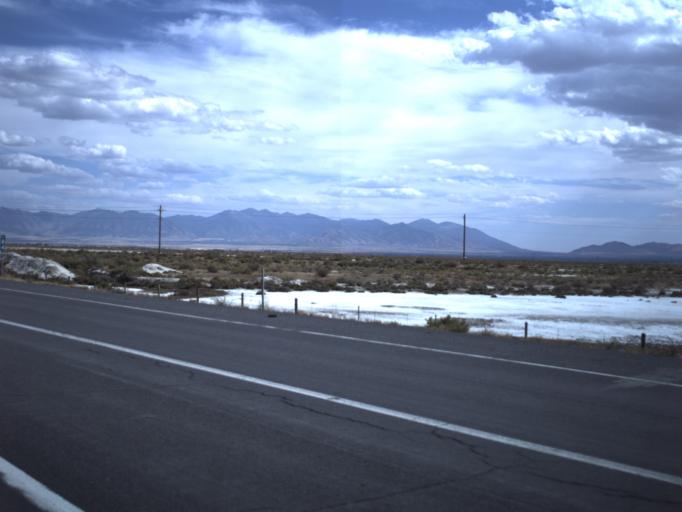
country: US
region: Utah
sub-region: Tooele County
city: Grantsville
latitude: 40.7059
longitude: -112.5195
